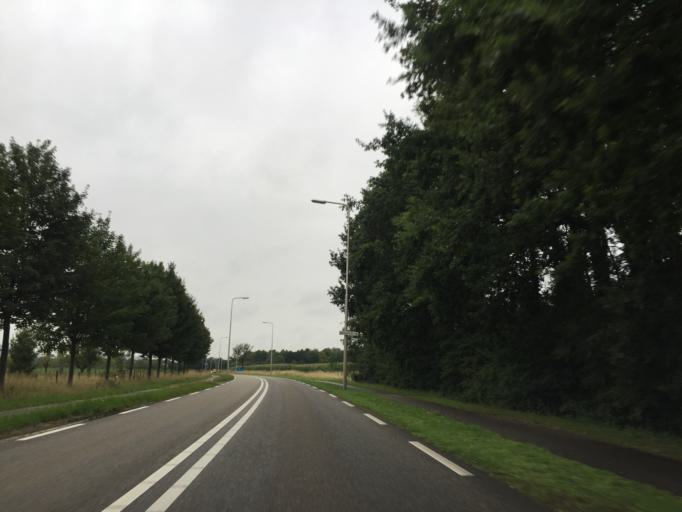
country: NL
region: Limburg
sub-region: Eijsden-Margraten
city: Eijsden
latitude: 50.7859
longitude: 5.7272
